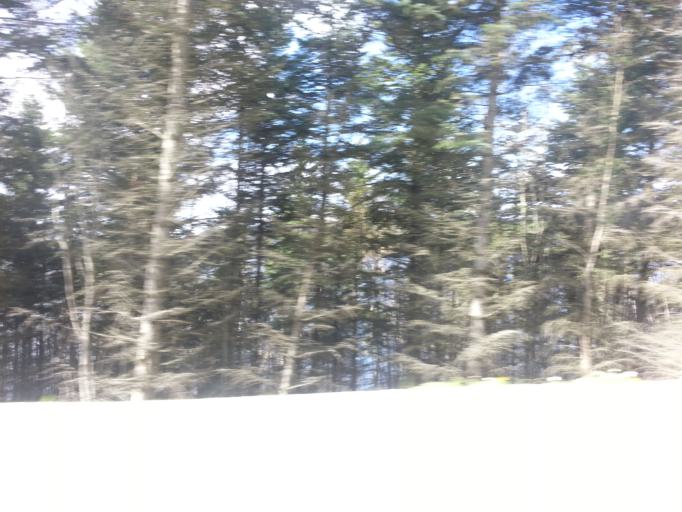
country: NO
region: Nord-Trondelag
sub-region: Levanger
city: Skogn
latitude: 63.6239
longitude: 11.1616
